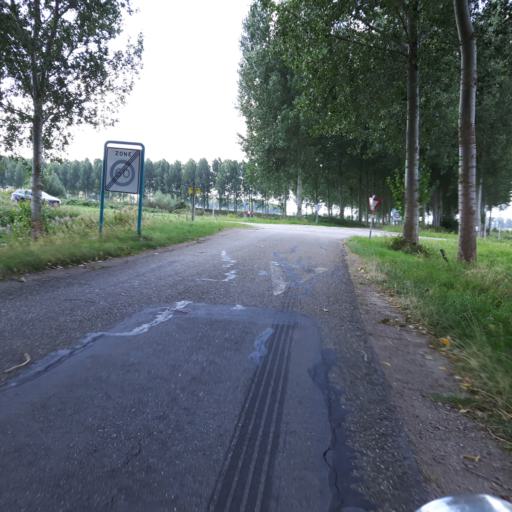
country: NL
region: Zeeland
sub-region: Gemeente Goes
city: Goes
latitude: 51.4643
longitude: 3.8380
